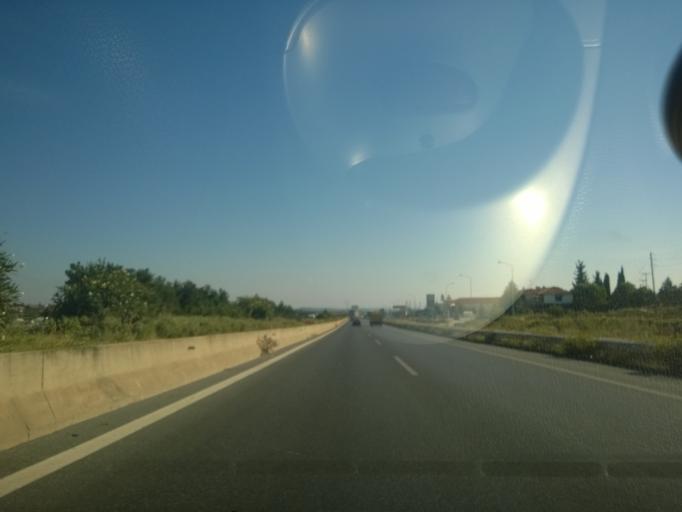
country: GR
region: Central Macedonia
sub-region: Nomos Thessalonikis
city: Kato Scholari
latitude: 40.4342
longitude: 23.0163
